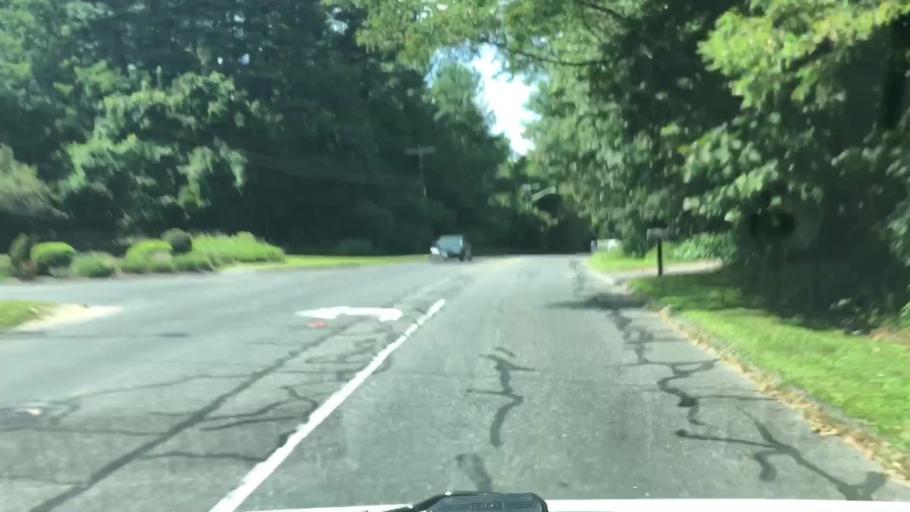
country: US
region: Massachusetts
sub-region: Hampshire County
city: Northampton
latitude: 42.3396
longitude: -72.6580
